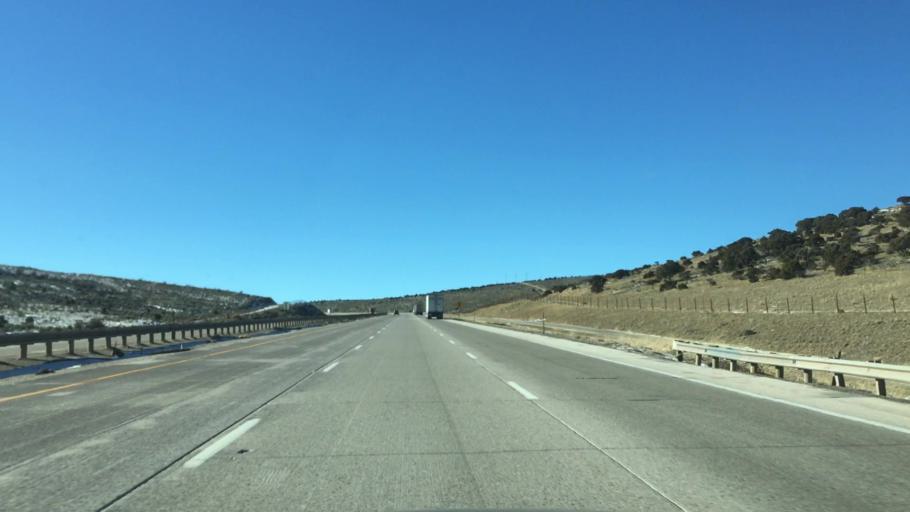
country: US
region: Wyoming
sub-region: Uinta County
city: Evanston
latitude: 41.2993
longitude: -110.6700
